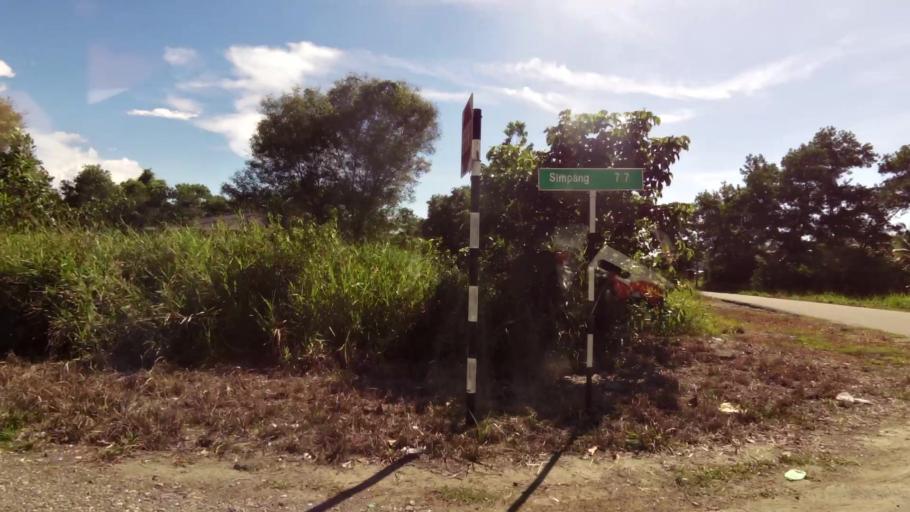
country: BN
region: Brunei and Muara
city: Bandar Seri Begawan
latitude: 4.9652
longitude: 114.9349
